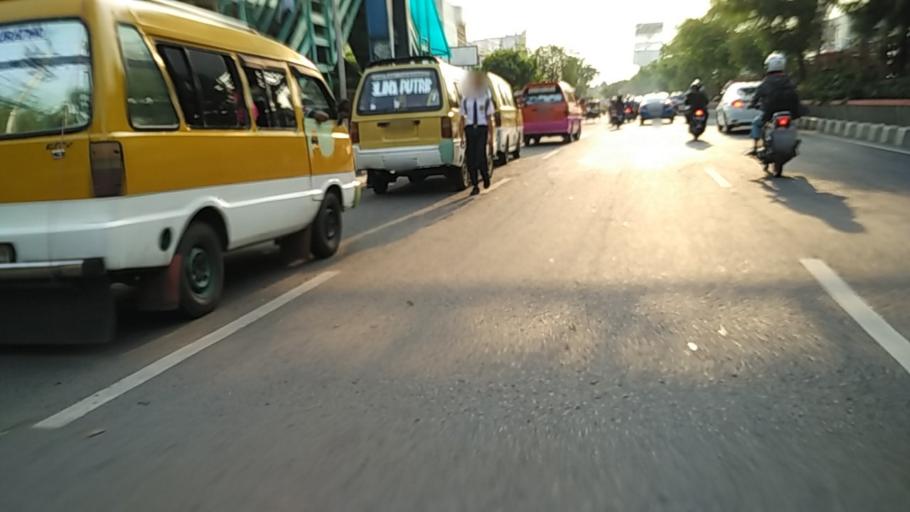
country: ID
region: Central Java
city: Semarang
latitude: -6.9817
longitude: 110.3952
